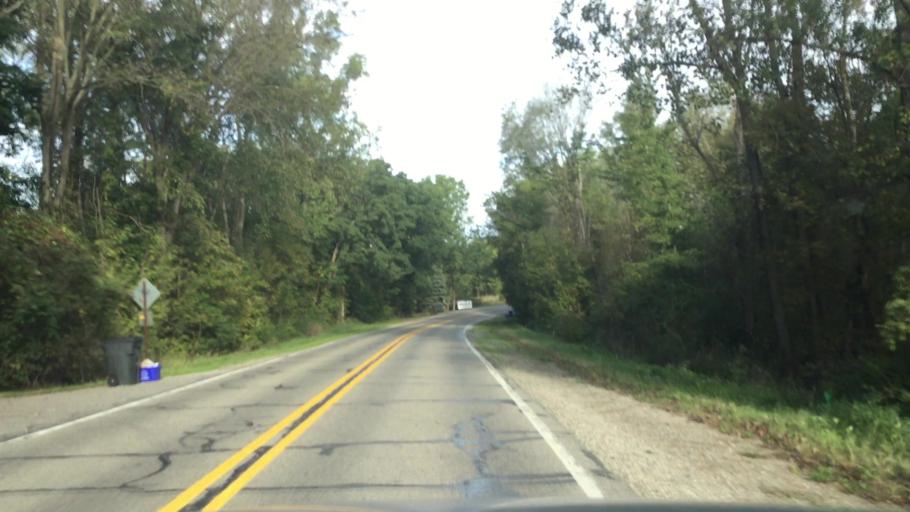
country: US
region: Michigan
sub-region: Livingston County
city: Howell
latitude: 42.5423
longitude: -83.8747
